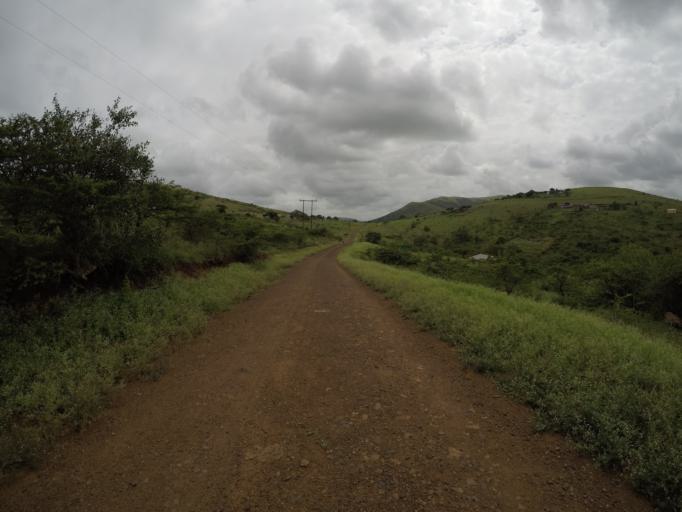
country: ZA
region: KwaZulu-Natal
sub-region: uThungulu District Municipality
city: Empangeni
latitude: -28.6220
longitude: 31.8911
